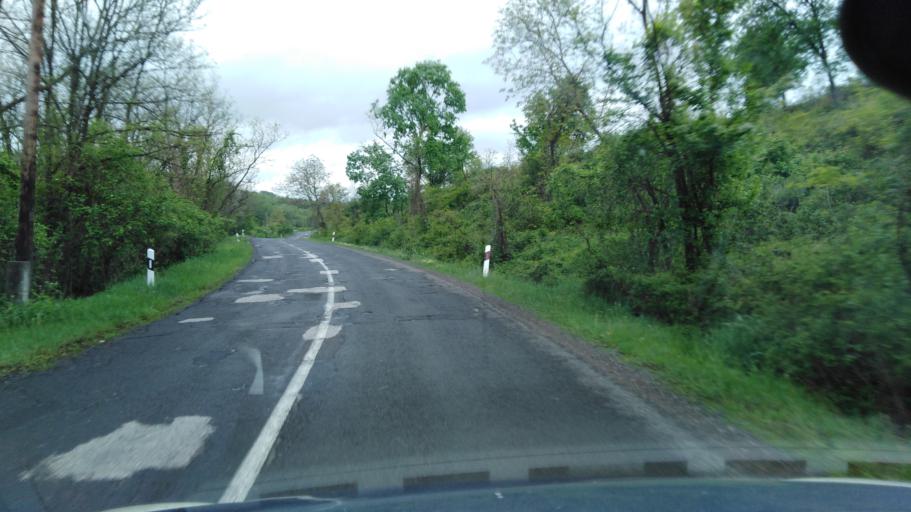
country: HU
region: Nograd
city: Rimoc
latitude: 48.0240
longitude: 19.5885
